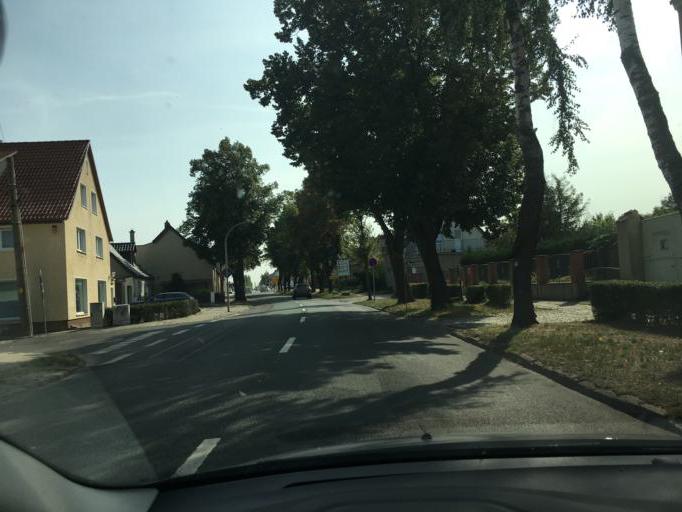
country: DE
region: Saxony-Anhalt
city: Calbe
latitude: 51.8931
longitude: 11.7702
